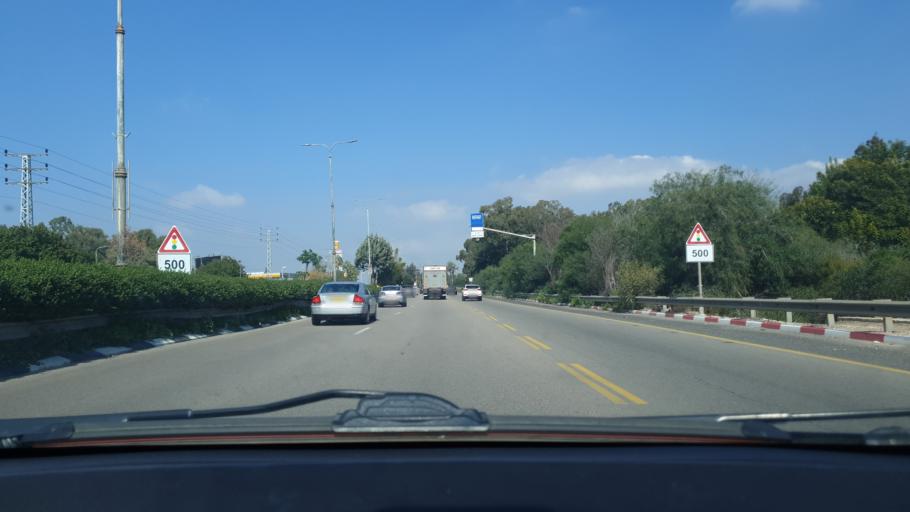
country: IL
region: Central District
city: Bet Dagan
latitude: 31.9887
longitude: 34.8120
